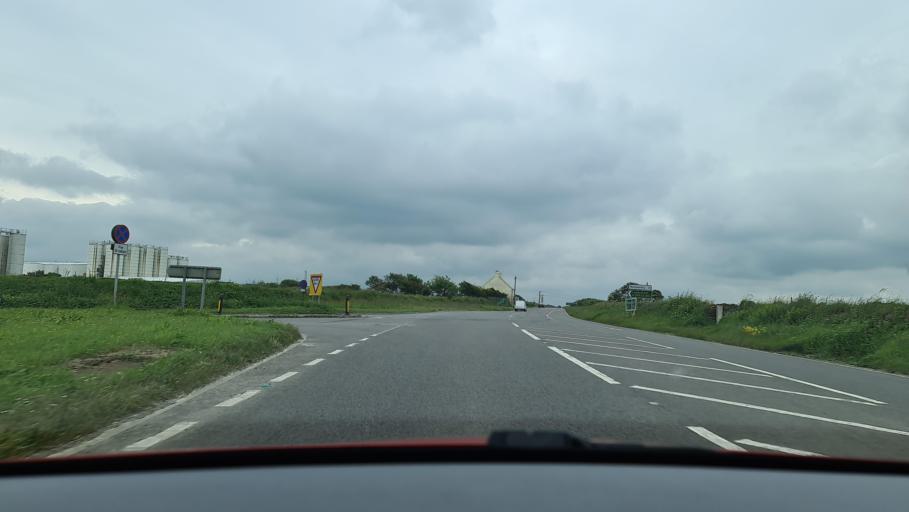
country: GB
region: England
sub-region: Cornwall
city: Camelford
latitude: 50.6518
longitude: -4.6362
